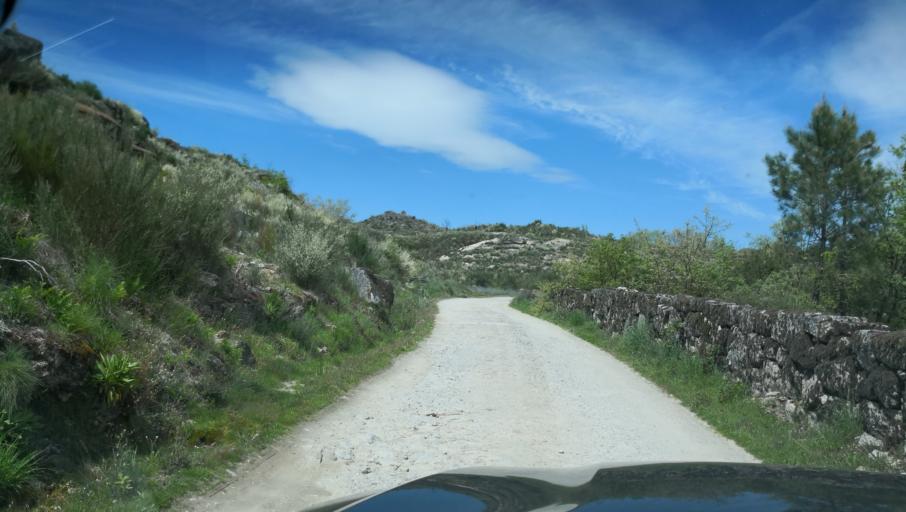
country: PT
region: Vila Real
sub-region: Vila Real
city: Vila Real
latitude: 41.3686
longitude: -7.6722
